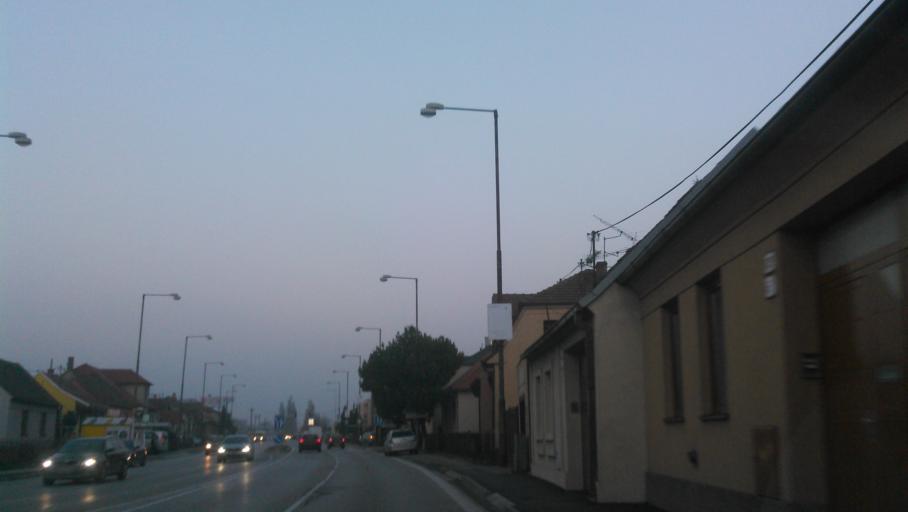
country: SK
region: Bratislavsky
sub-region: Okres Pezinok
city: Pezinok
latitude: 48.2726
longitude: 17.2517
